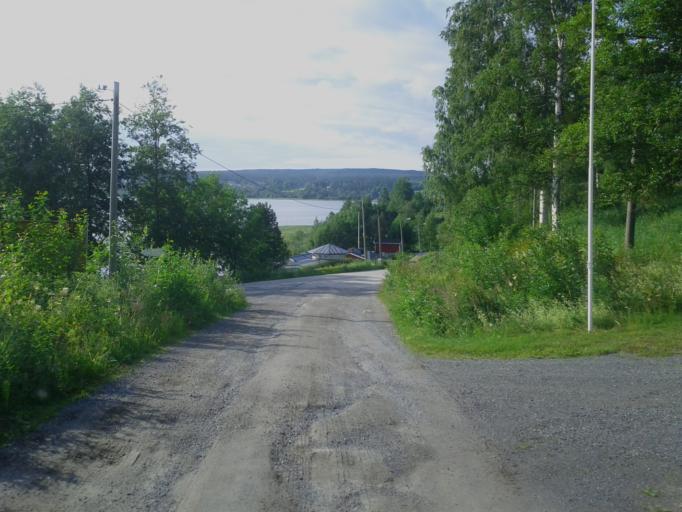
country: SE
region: Vaesternorrland
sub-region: OErnskoeldsviks Kommun
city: Ornskoldsvik
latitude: 63.2572
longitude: 18.8099
